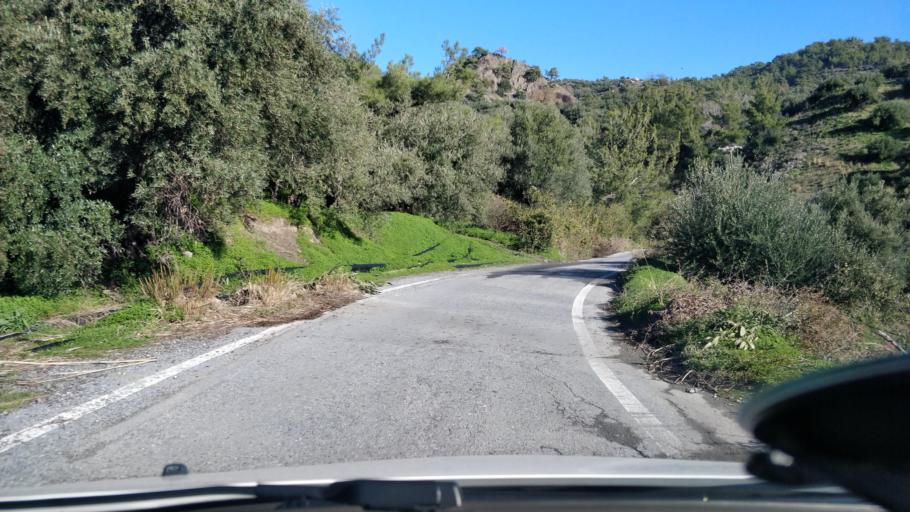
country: GR
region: Crete
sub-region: Nomos Lasithiou
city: Gra Liyia
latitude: 35.0502
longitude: 25.5795
